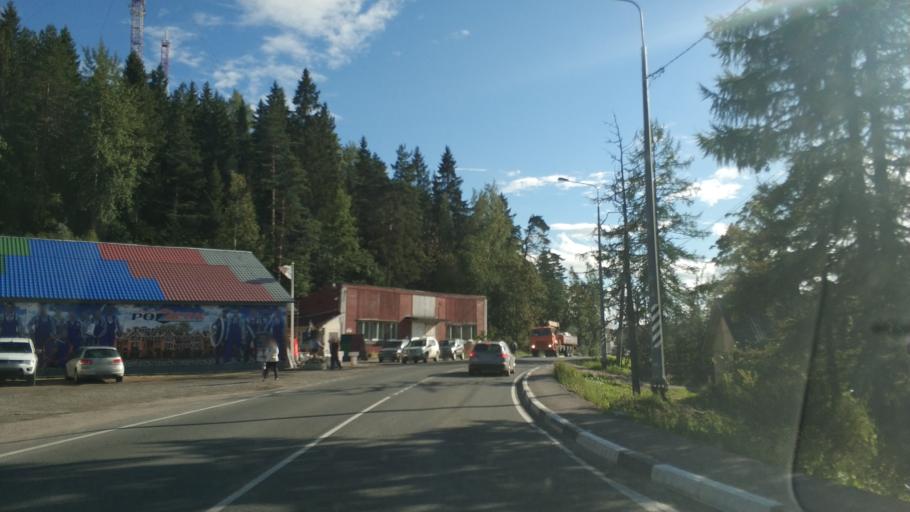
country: RU
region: Republic of Karelia
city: Lakhdenpokh'ya
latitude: 61.5257
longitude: 30.2015
